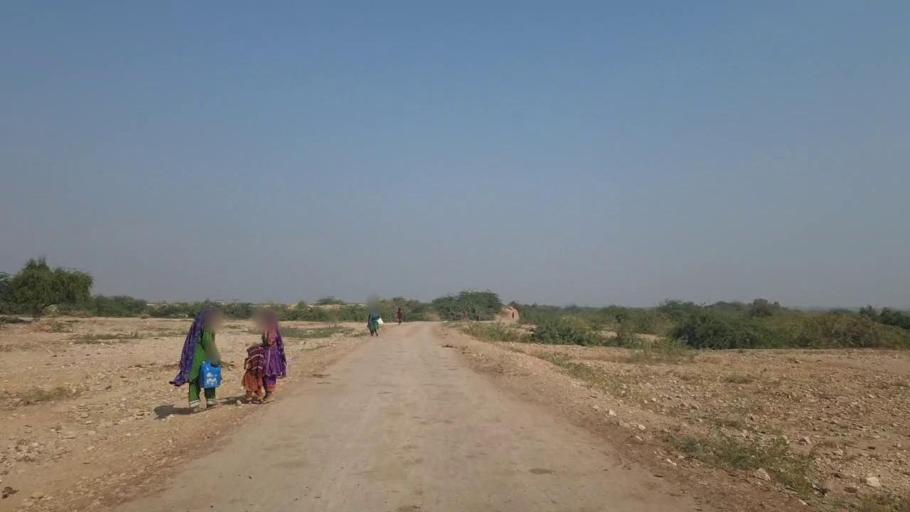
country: PK
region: Sindh
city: Matiari
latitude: 25.5448
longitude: 68.3522
